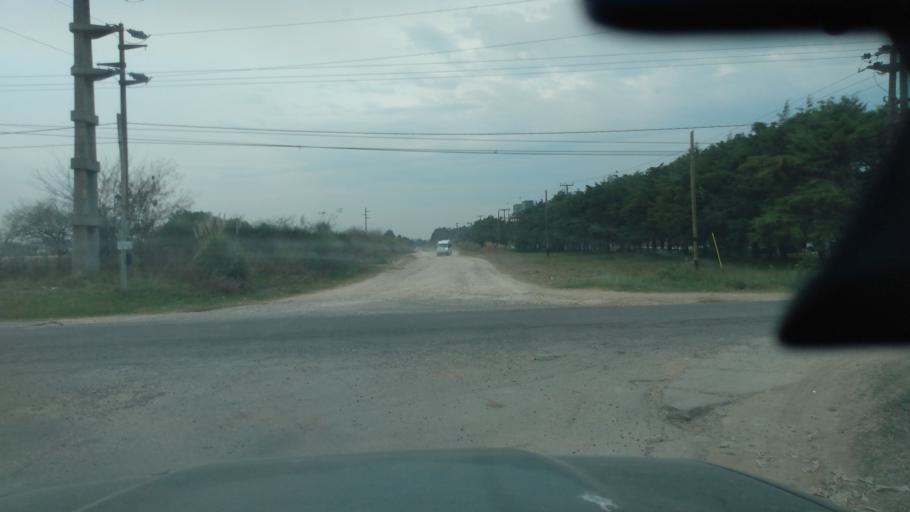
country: AR
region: Buenos Aires
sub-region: Partido de Lujan
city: Lujan
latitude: -34.5643
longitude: -59.1417
